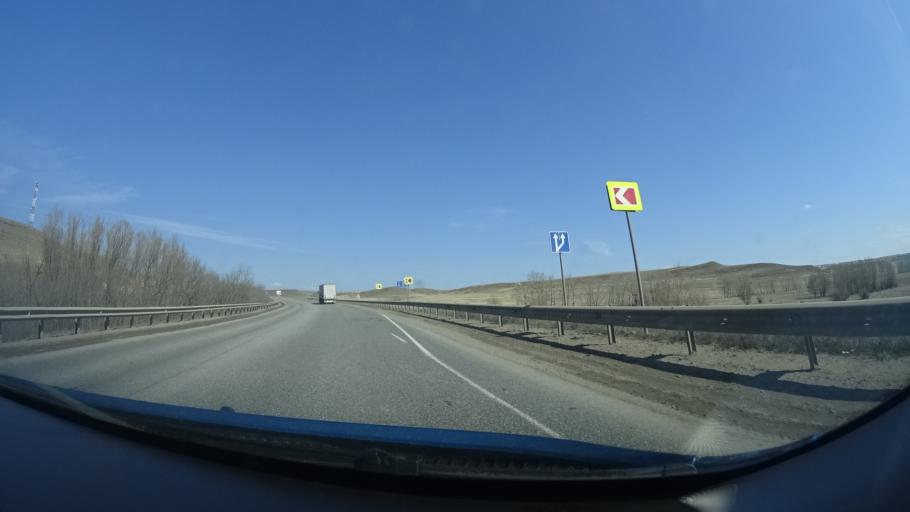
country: RU
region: Bashkortostan
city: Subkhankulovo
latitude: 54.4880
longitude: 53.9289
